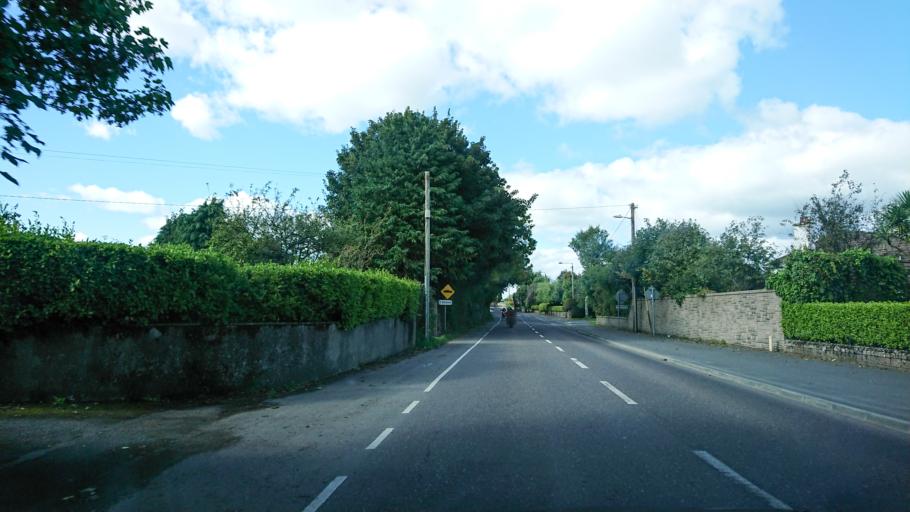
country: IE
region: Munster
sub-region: Waterford
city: Dungarvan
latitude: 52.0931
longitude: -7.6365
